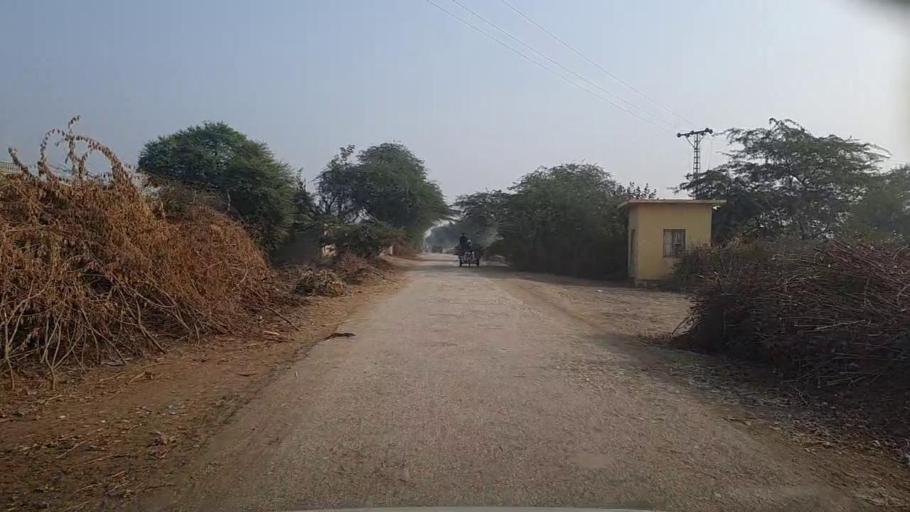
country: PK
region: Sindh
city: Kandiari
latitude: 27.0355
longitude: 68.4825
